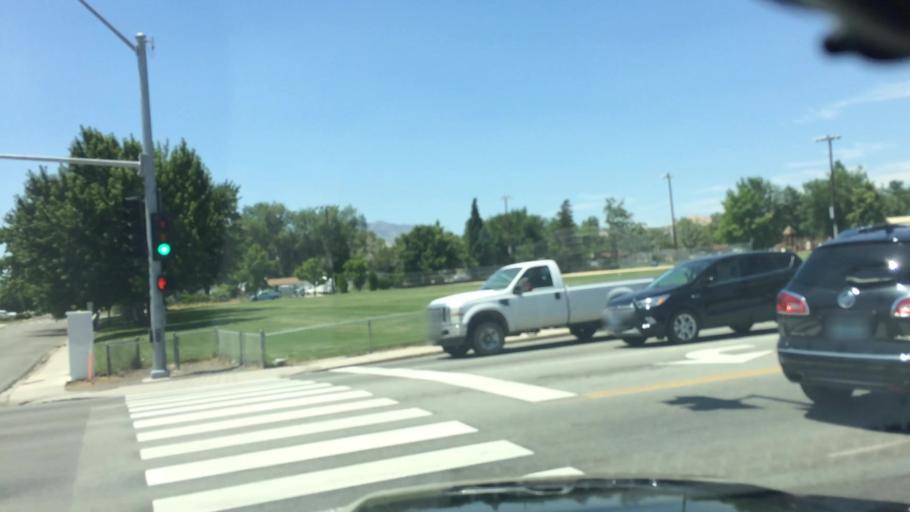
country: US
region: Nevada
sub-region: Washoe County
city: Sparks
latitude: 39.5474
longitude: -119.7526
